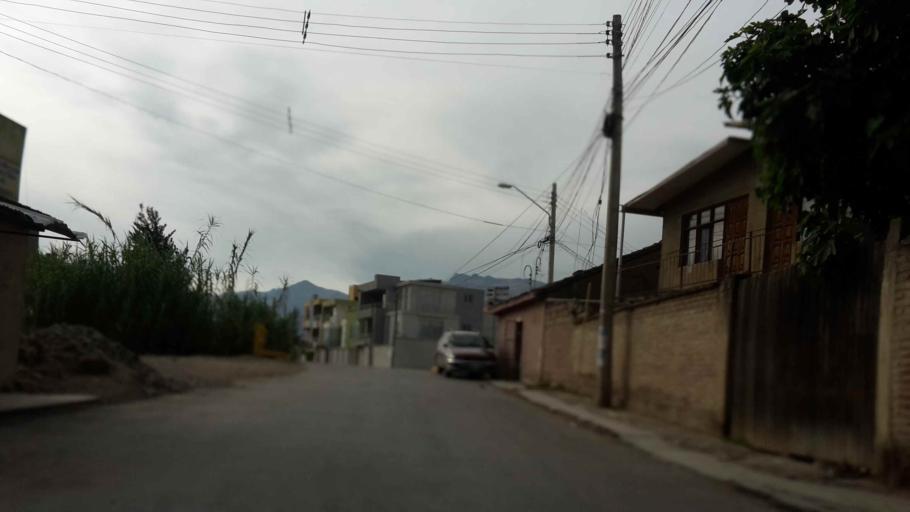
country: BO
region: Cochabamba
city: Cochabamba
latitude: -17.3609
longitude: -66.1908
